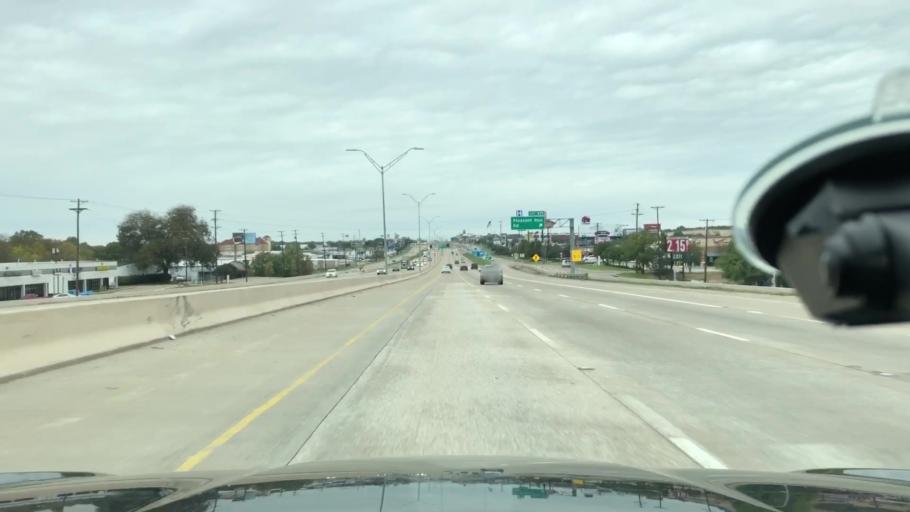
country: US
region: Texas
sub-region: Dallas County
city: DeSoto
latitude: 32.5915
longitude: -96.8224
